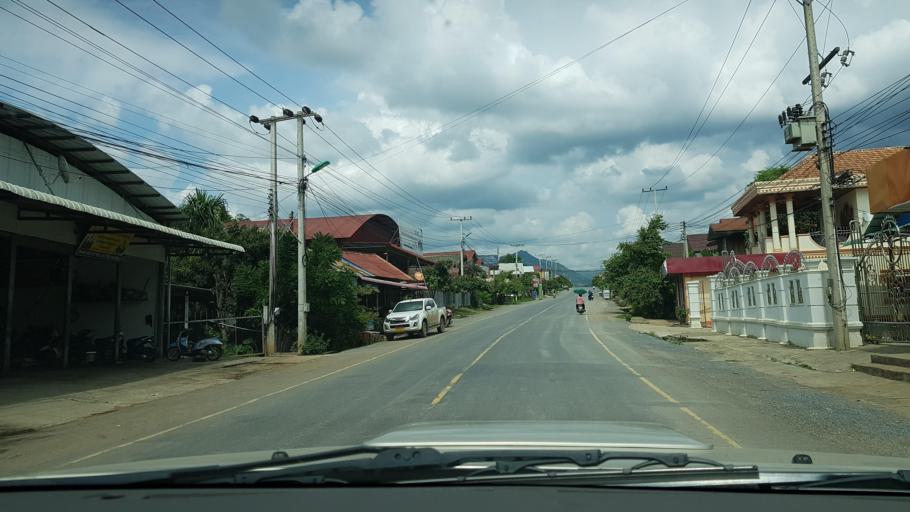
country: LA
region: Loungnamtha
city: Muang Nale
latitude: 20.1473
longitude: 101.4614
